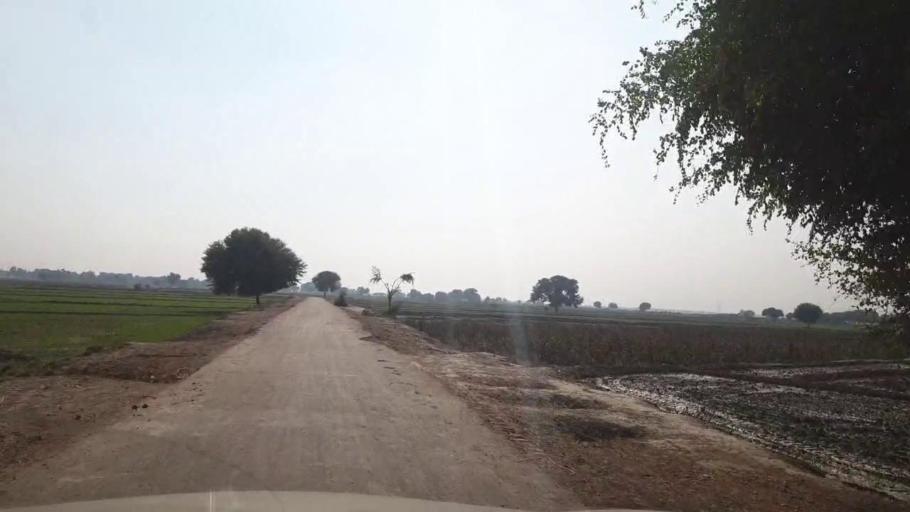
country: PK
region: Sindh
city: Bhan
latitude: 26.5389
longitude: 67.7629
